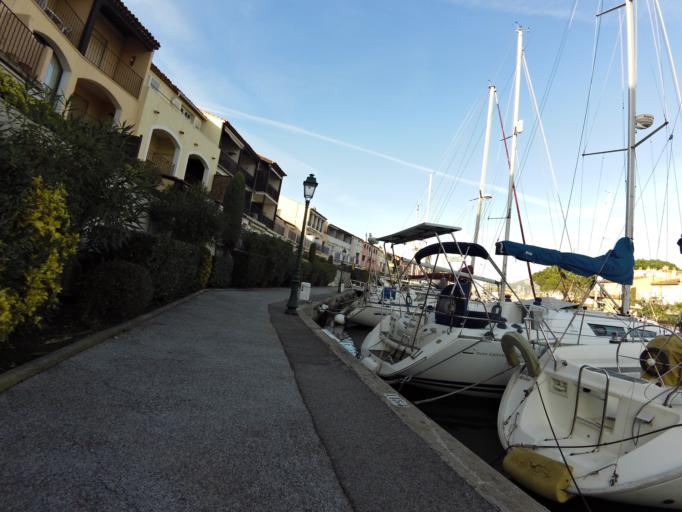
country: FR
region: Provence-Alpes-Cote d'Azur
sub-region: Departement du Var
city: Gassin
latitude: 43.2703
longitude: 6.5742
